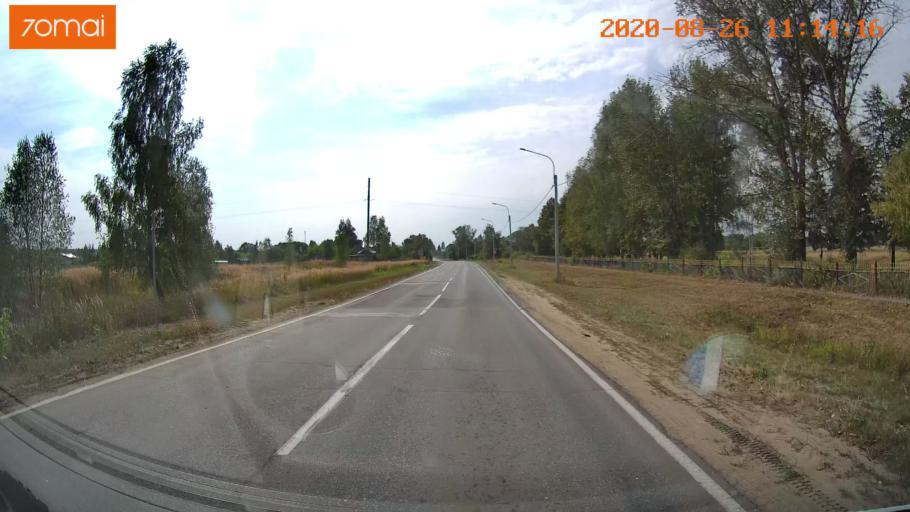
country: RU
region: Rjazan
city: Izhevskoye
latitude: 54.4504
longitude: 41.1175
